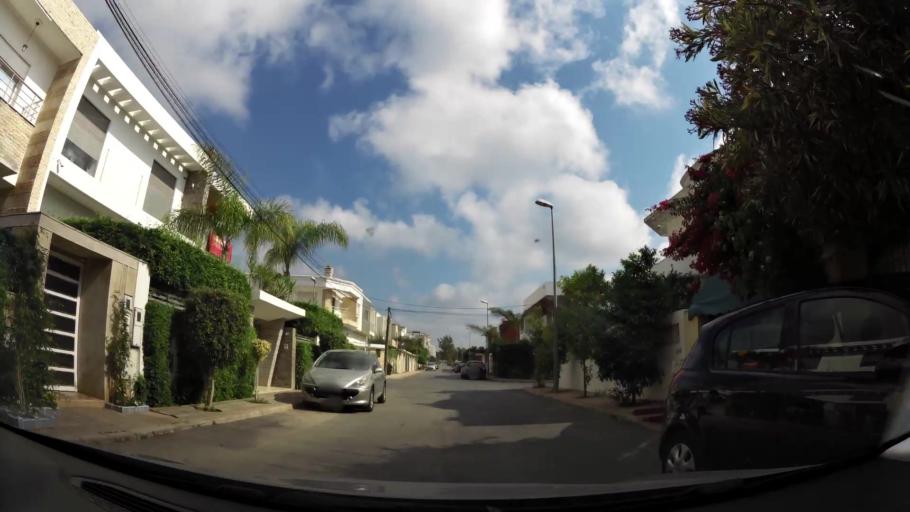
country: MA
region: Rabat-Sale-Zemmour-Zaer
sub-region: Skhirate-Temara
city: Temara
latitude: 33.9513
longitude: -6.8745
